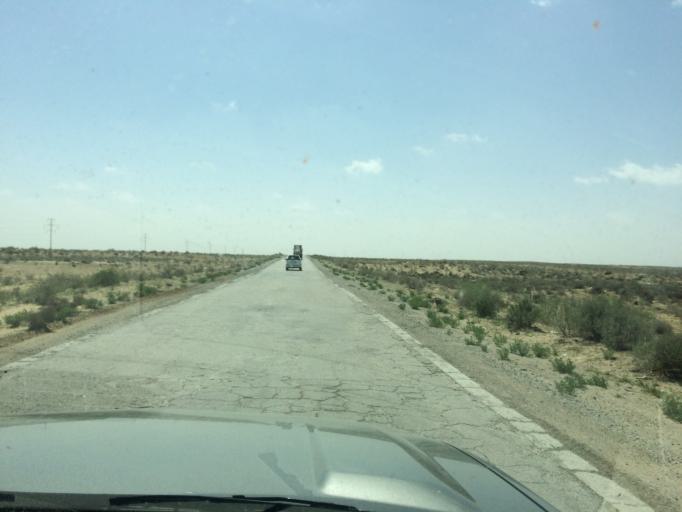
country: TM
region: Balkan
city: Gumdag
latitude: 38.8054
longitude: 54.5981
